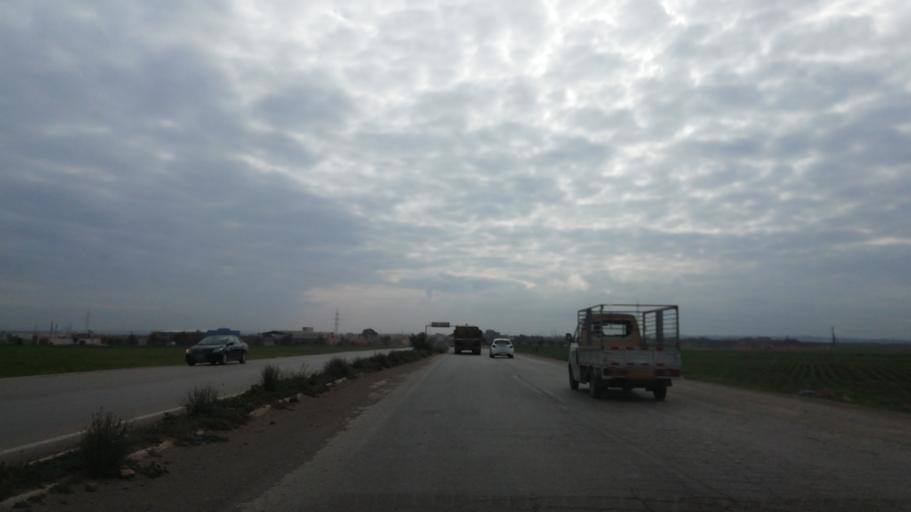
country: DZ
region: Oran
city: Ain el Bya
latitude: 35.7961
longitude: -0.3440
